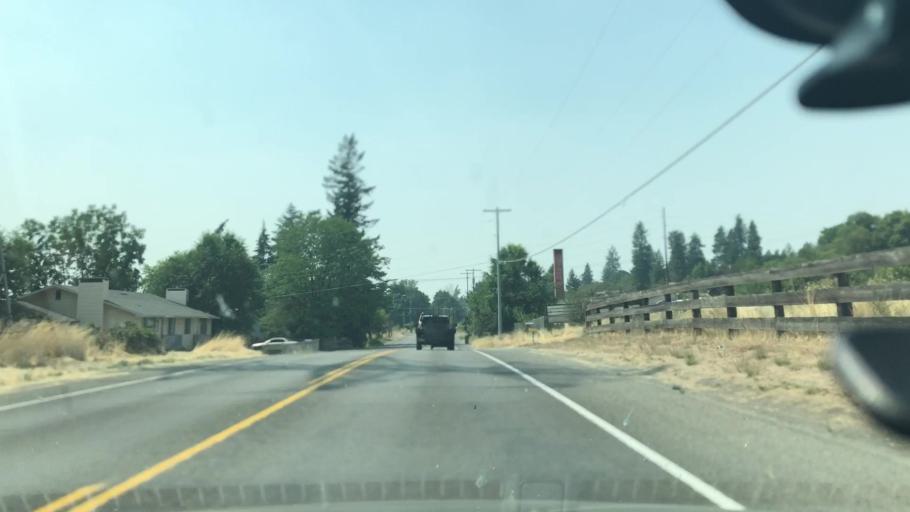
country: US
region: Washington
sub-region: Spokane County
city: Millwood
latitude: 47.6856
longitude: -117.3416
